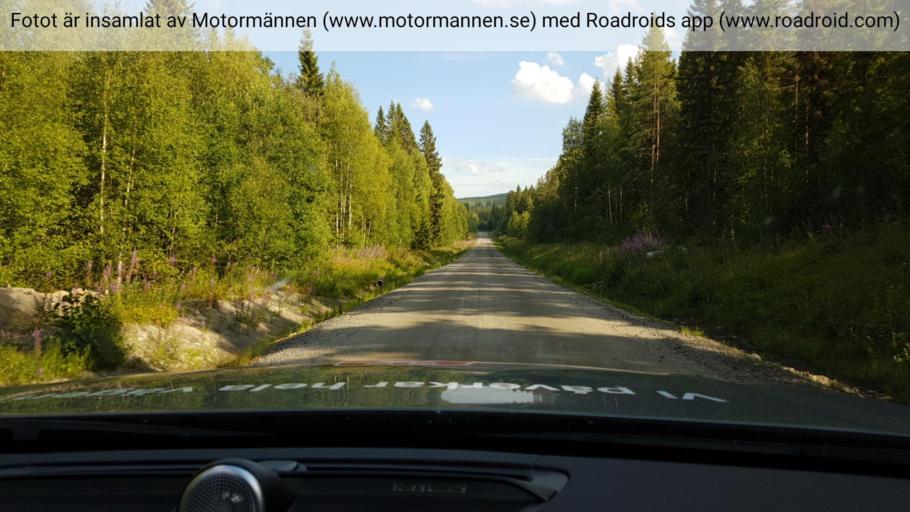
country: SE
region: Vaesterbotten
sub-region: Dorotea Kommun
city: Dorotea
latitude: 63.9267
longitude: 16.1694
